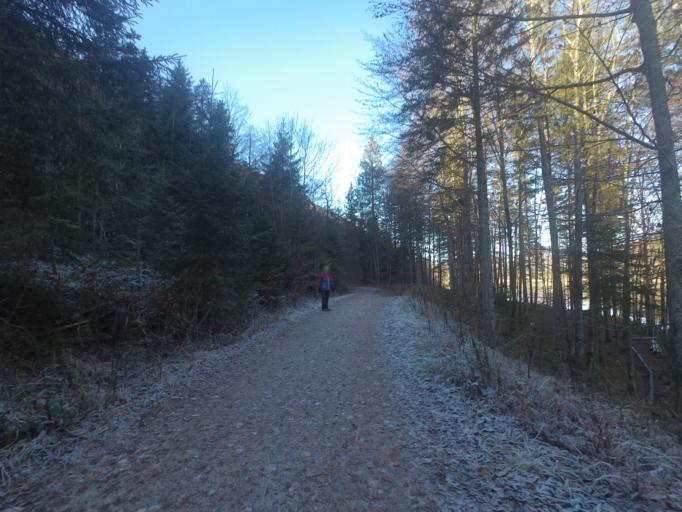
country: AT
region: Salzburg
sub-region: Politischer Bezirk Salzburg-Umgebung
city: Faistenau
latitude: 47.7423
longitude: 13.2499
